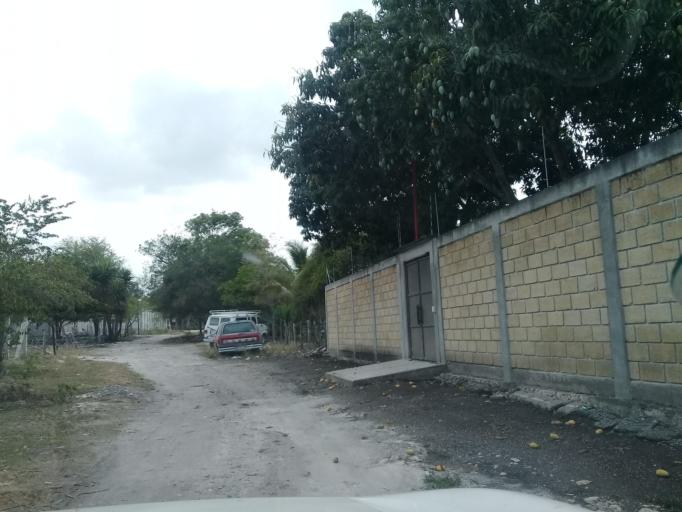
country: MX
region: Veracruz
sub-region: Emiliano Zapata
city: Plan del Rio
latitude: 19.3571
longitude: -96.6591
